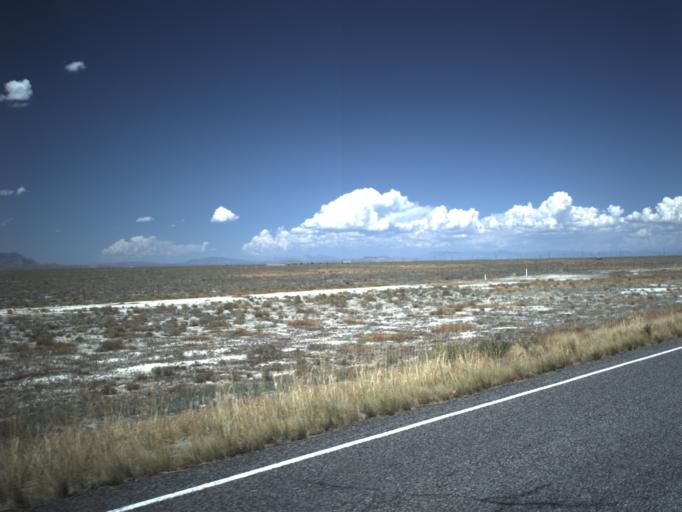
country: US
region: Utah
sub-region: Millard County
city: Delta
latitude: 39.2239
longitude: -112.9429
